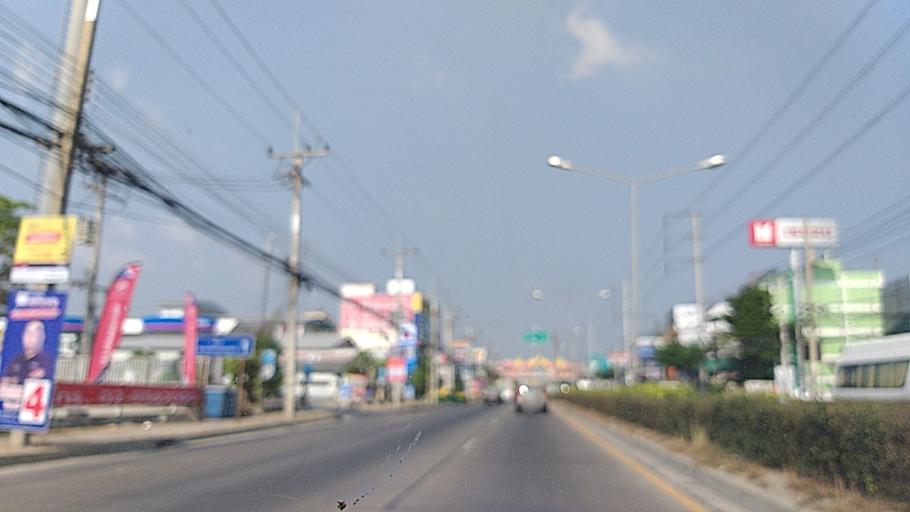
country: TH
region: Bangkok
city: Sai Mai
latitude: 13.9325
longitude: 100.6777
